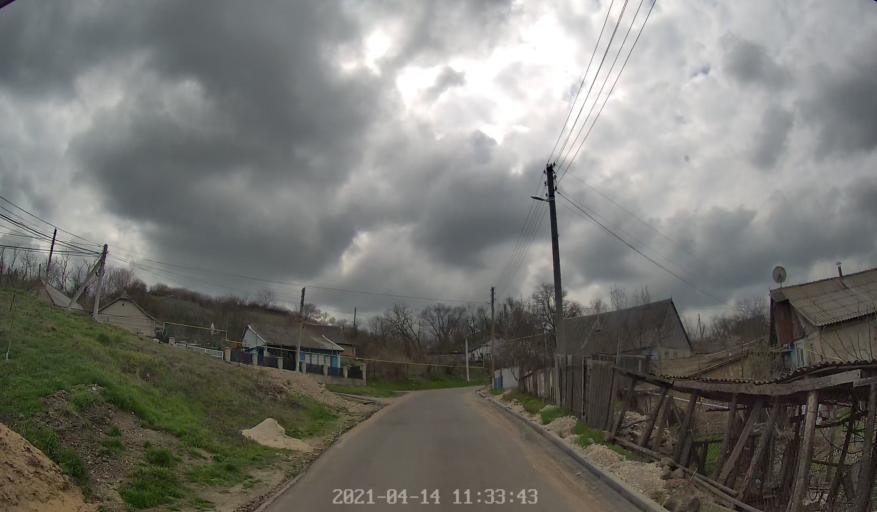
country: MD
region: Criuleni
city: Criuleni
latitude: 47.1784
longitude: 29.1648
